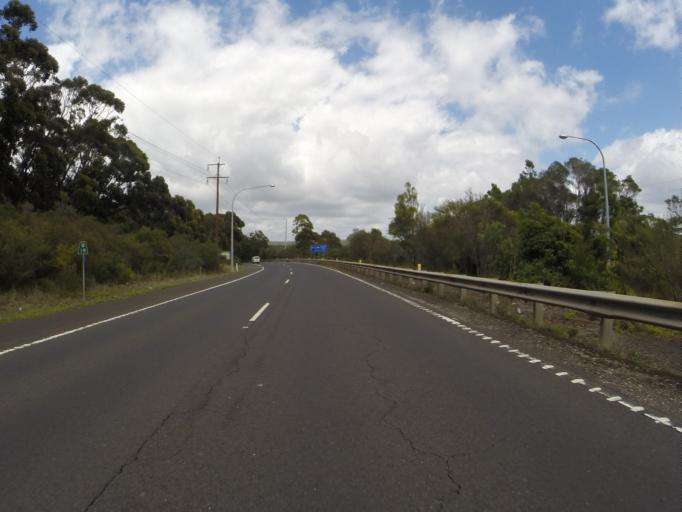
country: AU
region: New South Wales
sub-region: Wollongong
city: Bulli
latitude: -34.3037
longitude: 150.9068
